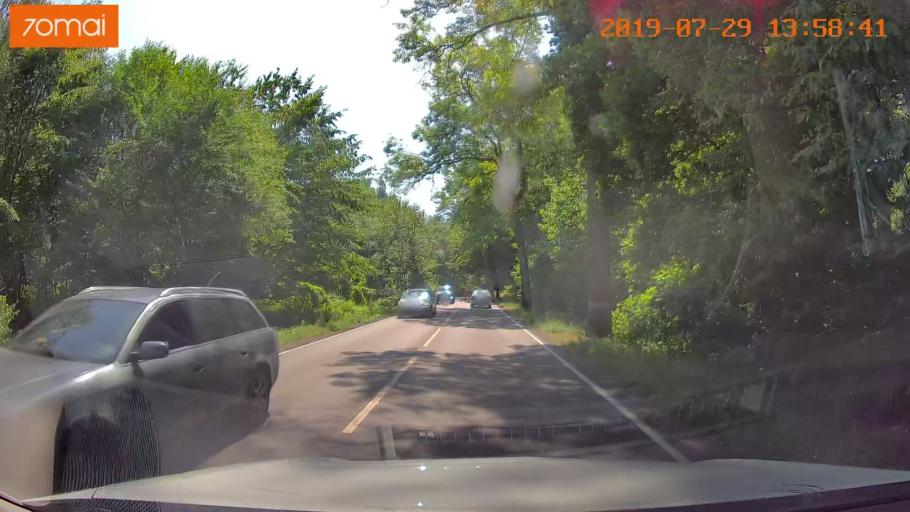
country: RU
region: Kaliningrad
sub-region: Gorod Kaliningrad
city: Baltiysk
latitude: 54.6912
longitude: 19.9358
